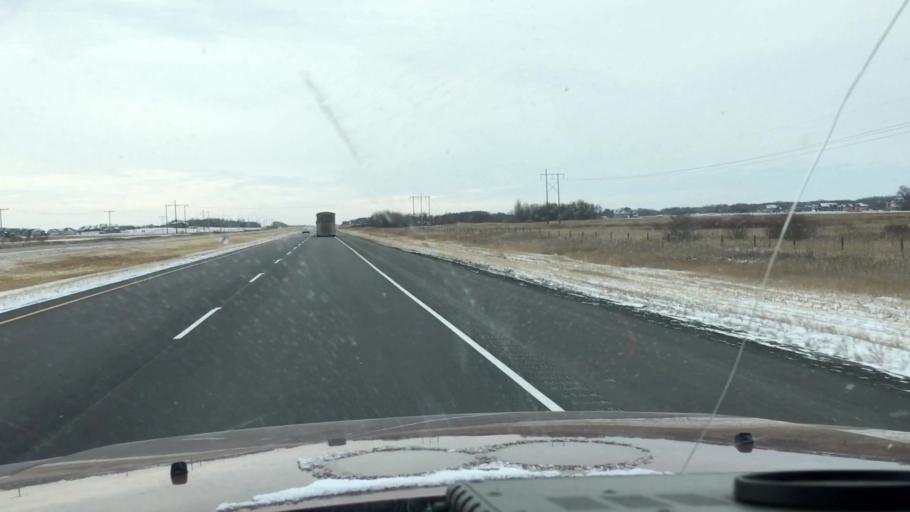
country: CA
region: Saskatchewan
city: Saskatoon
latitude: 51.9525
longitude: -106.5458
